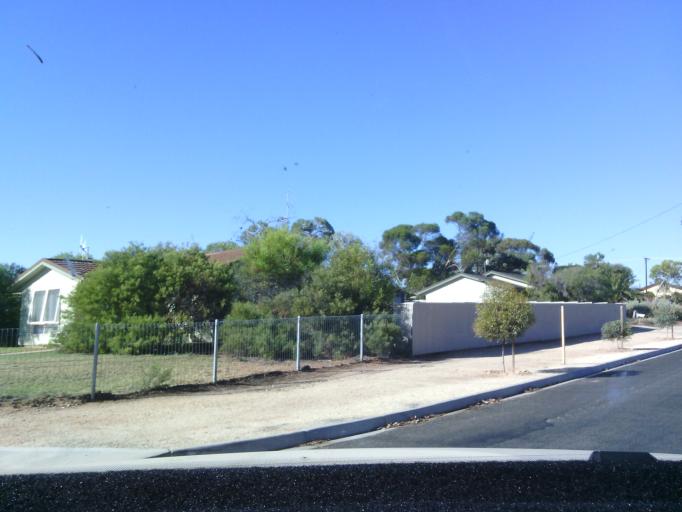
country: AU
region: South Australia
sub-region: Berri and Barmera
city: Berri
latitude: -34.2710
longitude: 140.6051
